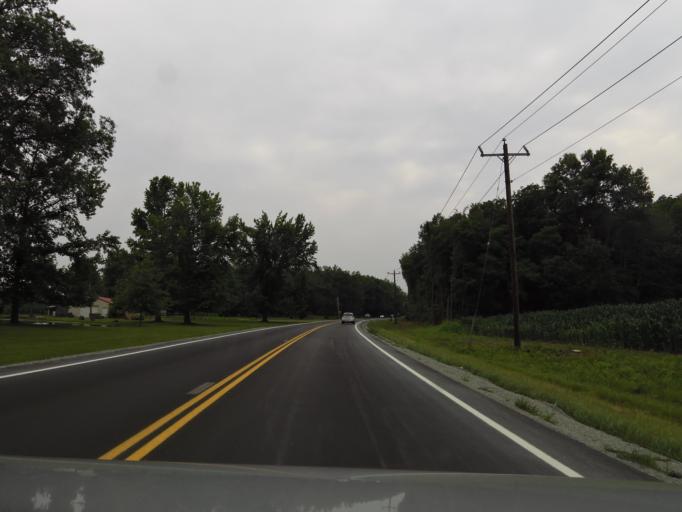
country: US
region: Ohio
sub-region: Clinton County
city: Blanchester
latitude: 39.2178
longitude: -83.9117
